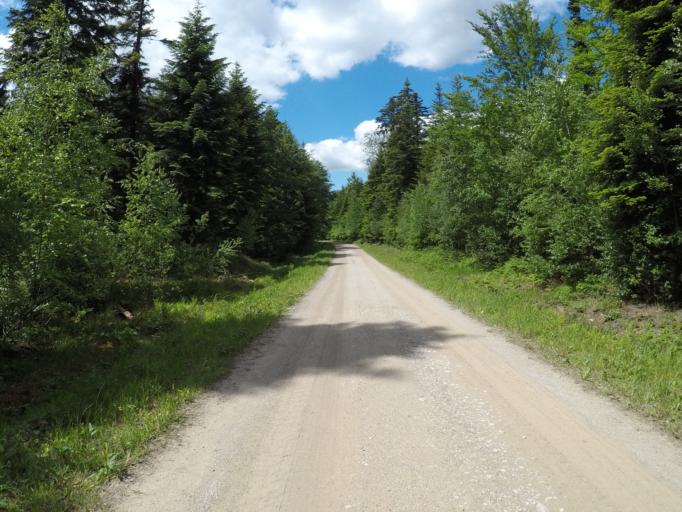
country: PL
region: Swietokrzyskie
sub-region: Powiat kielecki
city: Zagnansk
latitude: 50.9325
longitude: 20.6468
